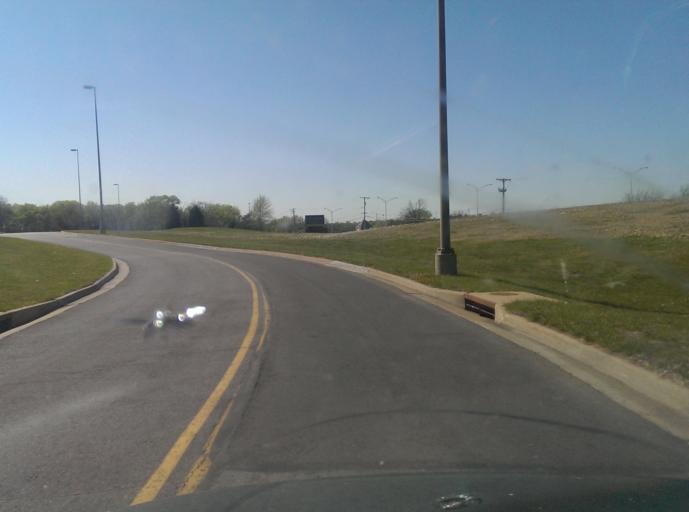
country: US
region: Kansas
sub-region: Johnson County
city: Lenexa
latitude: 38.9266
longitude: -94.7265
